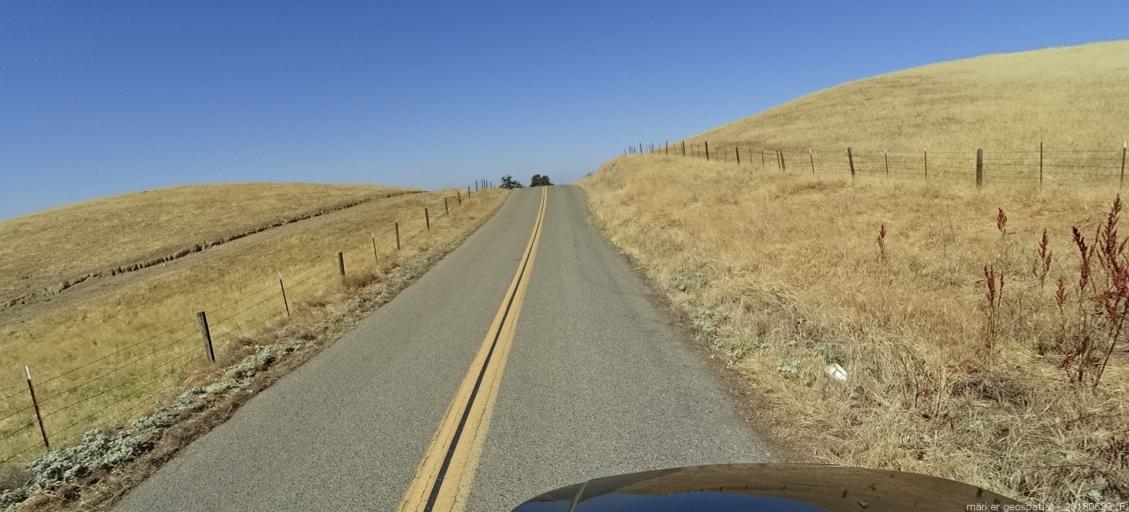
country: US
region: California
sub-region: Madera County
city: Bonadelle Ranchos-Madera Ranchos
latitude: 37.0746
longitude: -119.8410
